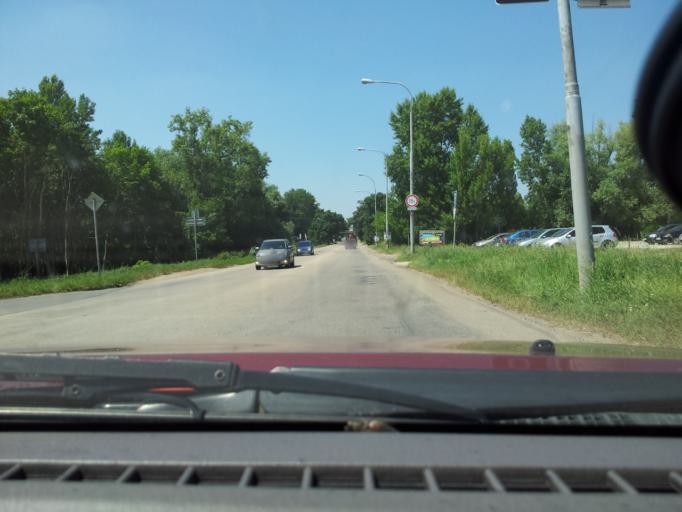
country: CZ
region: South Moravian
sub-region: Mesto Brno
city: Brno
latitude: 49.1582
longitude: 16.6437
